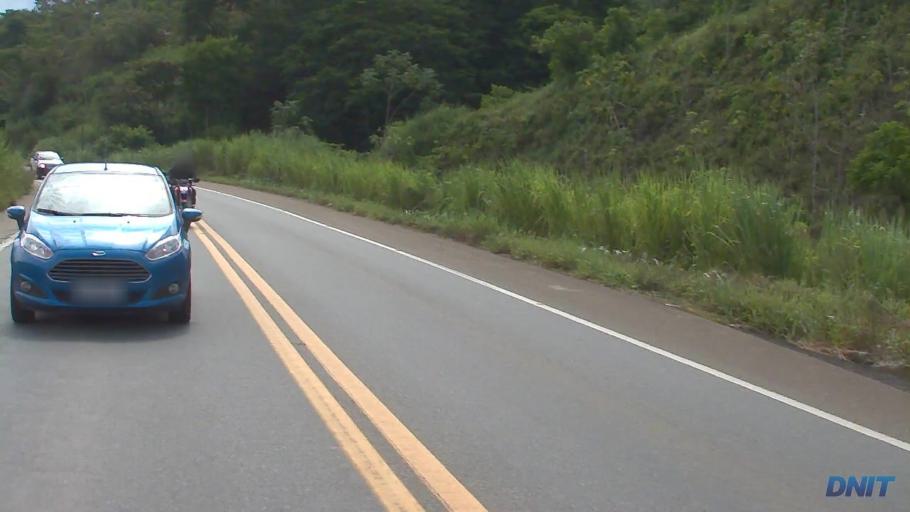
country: BR
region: Minas Gerais
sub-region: Ipaba
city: Ipaba
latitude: -19.3636
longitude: -42.4486
